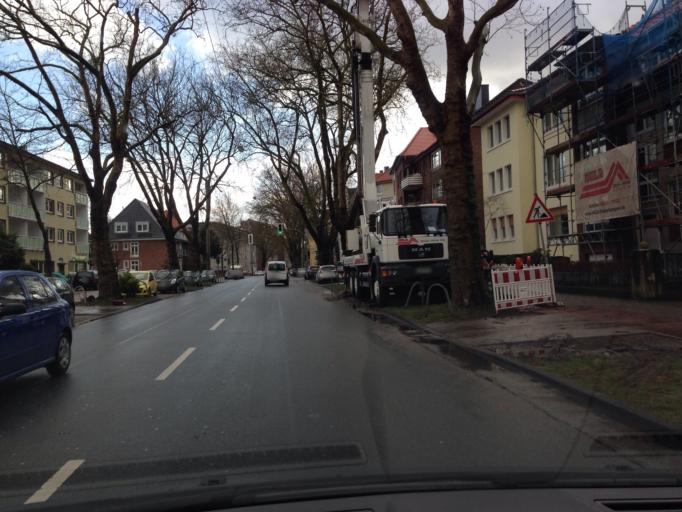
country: DE
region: North Rhine-Westphalia
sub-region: Regierungsbezirk Munster
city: Muenster
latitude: 51.9578
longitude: 7.6471
